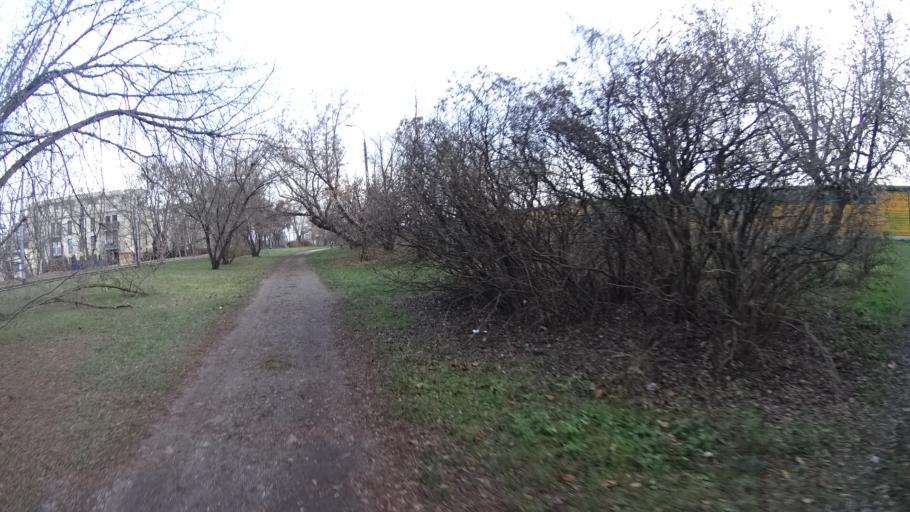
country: PL
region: Masovian Voivodeship
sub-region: Warszawa
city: Bemowo
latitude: 52.2475
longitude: 20.9181
